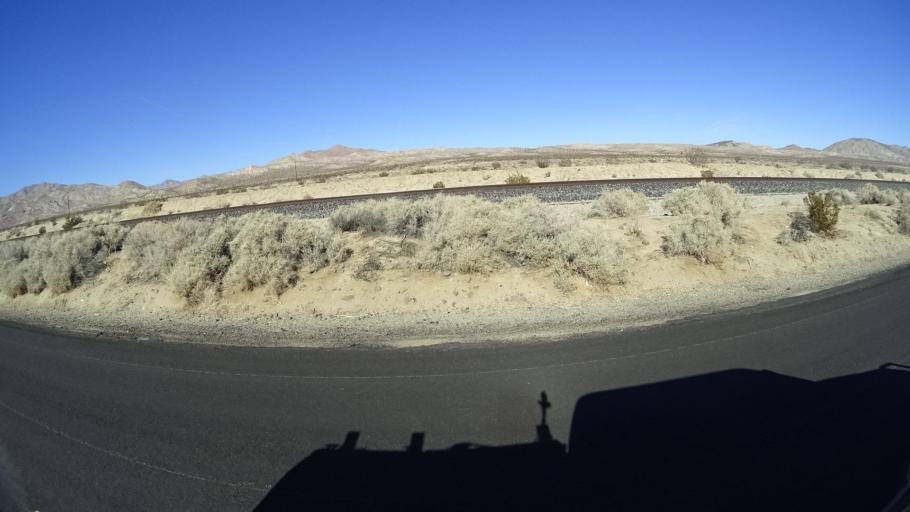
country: US
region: California
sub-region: Kern County
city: California City
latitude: 35.2990
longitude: -117.9841
